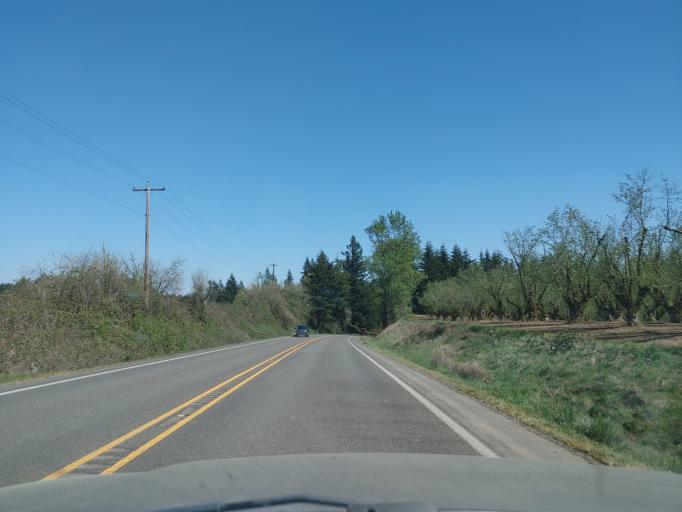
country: US
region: Oregon
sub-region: Marion County
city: Woodburn
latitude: 45.2342
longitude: -122.8975
